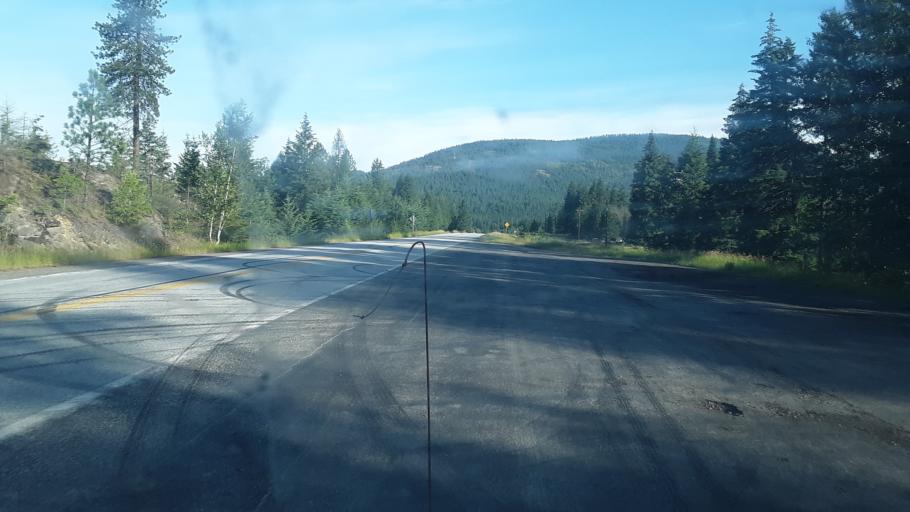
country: US
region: Idaho
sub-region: Boundary County
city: Bonners Ferry
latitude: 48.7234
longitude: -116.1704
